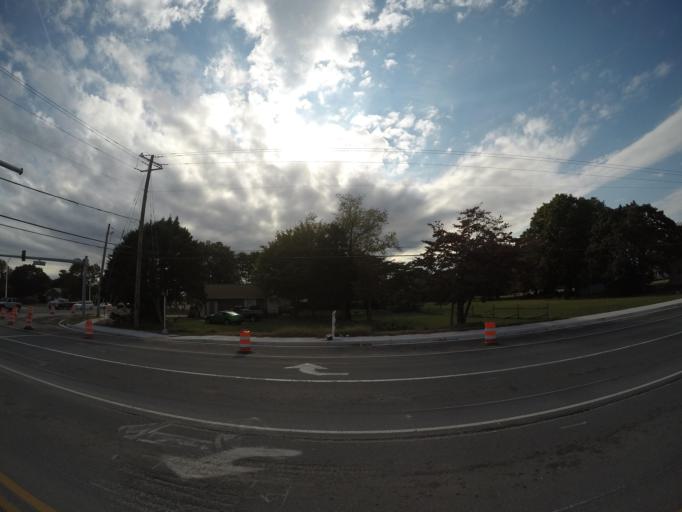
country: US
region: Delaware
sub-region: Sussex County
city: Lewes
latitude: 38.7241
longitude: -75.1427
